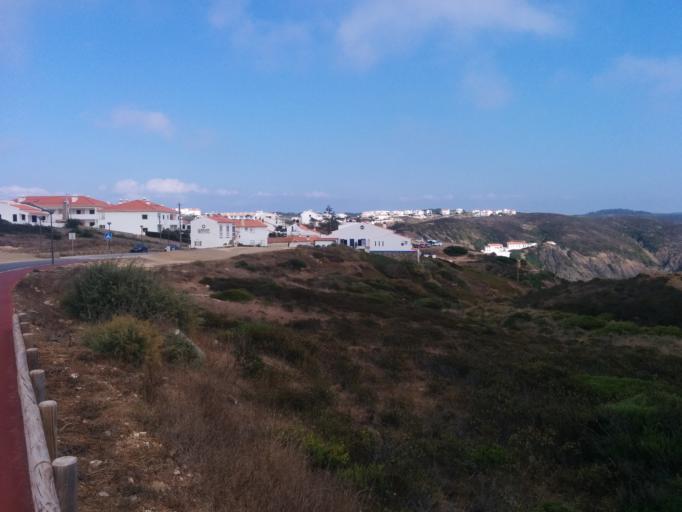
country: PT
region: Faro
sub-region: Aljezur
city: Aljezur
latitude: 37.2969
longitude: -8.8707
